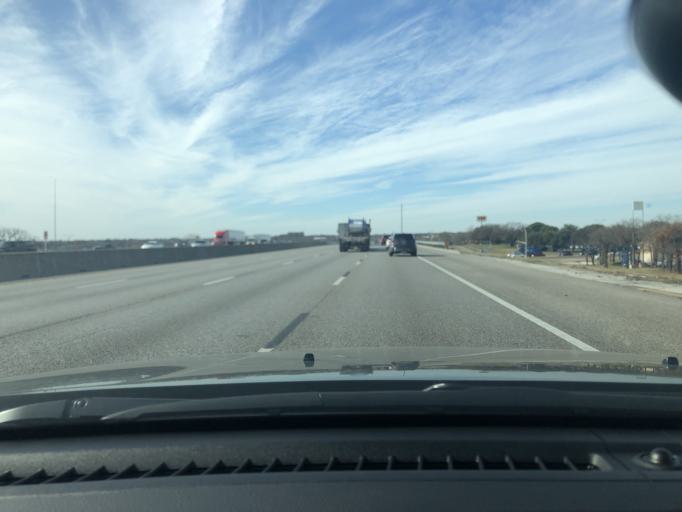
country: US
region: Texas
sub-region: Tarrant County
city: Dalworthington Gardens
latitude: 32.6747
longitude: -97.1475
